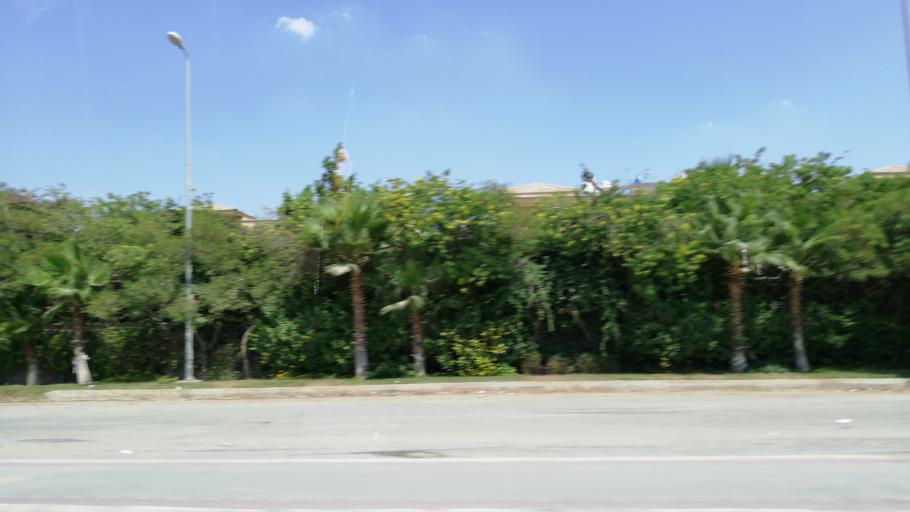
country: EG
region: Muhafazat al Qalyubiyah
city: Al Khankah
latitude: 30.0518
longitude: 31.4752
